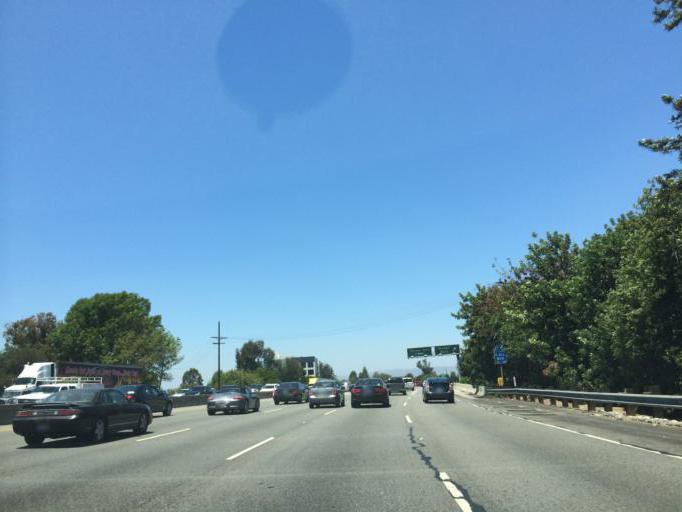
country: US
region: California
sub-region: Los Angeles County
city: Northridge
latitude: 34.1718
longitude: -118.5312
